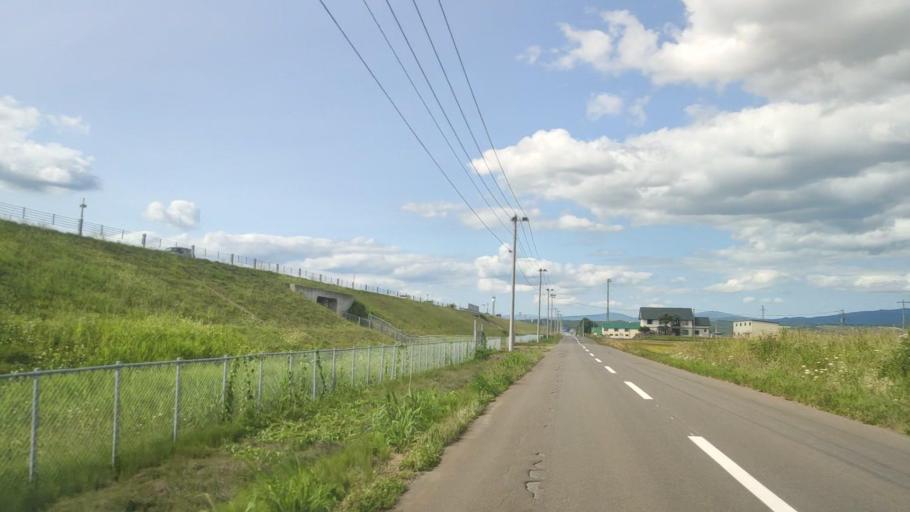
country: JP
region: Hokkaido
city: Nayoro
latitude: 44.3546
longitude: 142.4362
